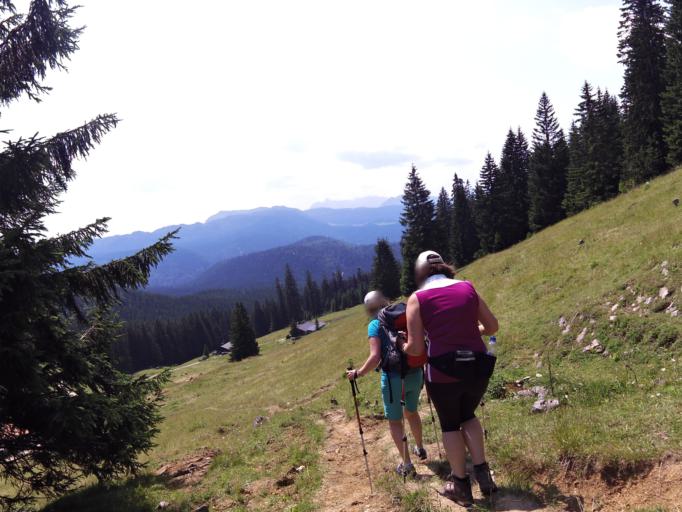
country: AT
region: Tyrol
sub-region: Politischer Bezirk Kitzbuhel
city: Waidring
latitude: 47.6689
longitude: 12.5931
